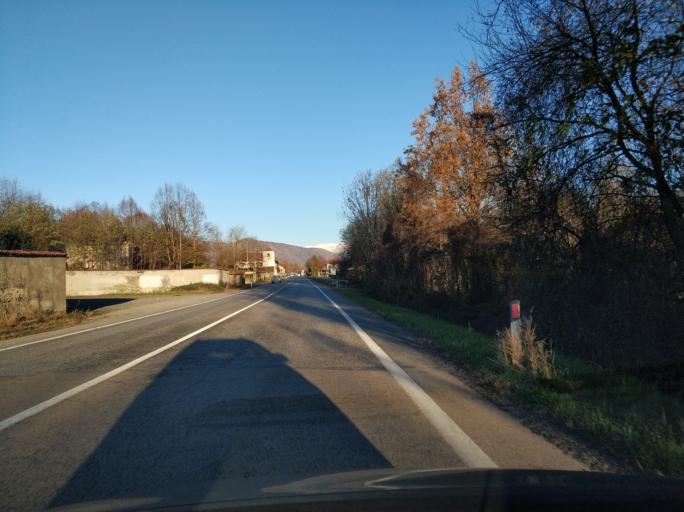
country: IT
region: Piedmont
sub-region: Provincia di Torino
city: Robassomero
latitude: 45.1832
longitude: 7.5748
